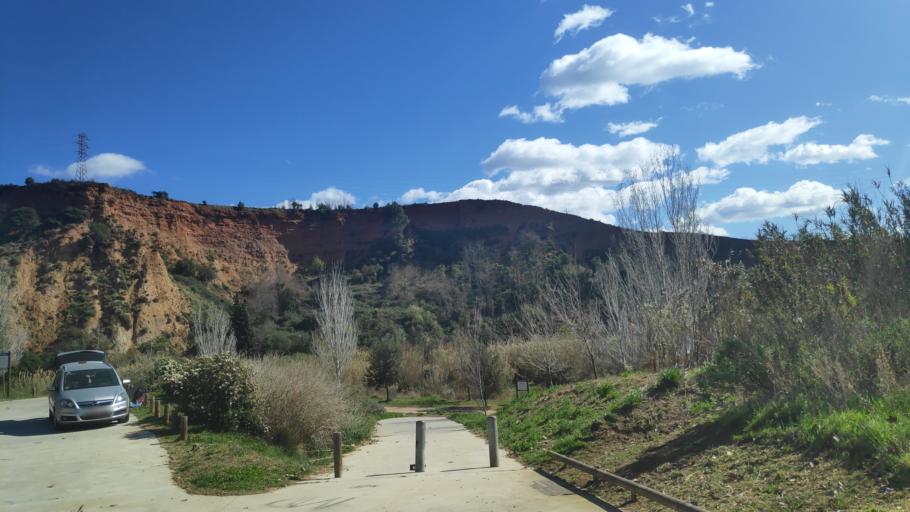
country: ES
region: Catalonia
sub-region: Provincia de Barcelona
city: Sabadell
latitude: 41.5643
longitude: 2.1087
